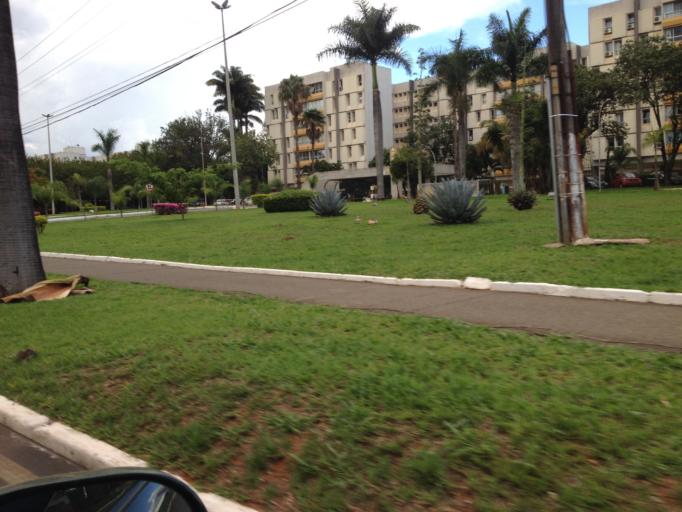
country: BR
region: Federal District
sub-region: Brasilia
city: Brasilia
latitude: -15.8096
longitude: -47.9450
